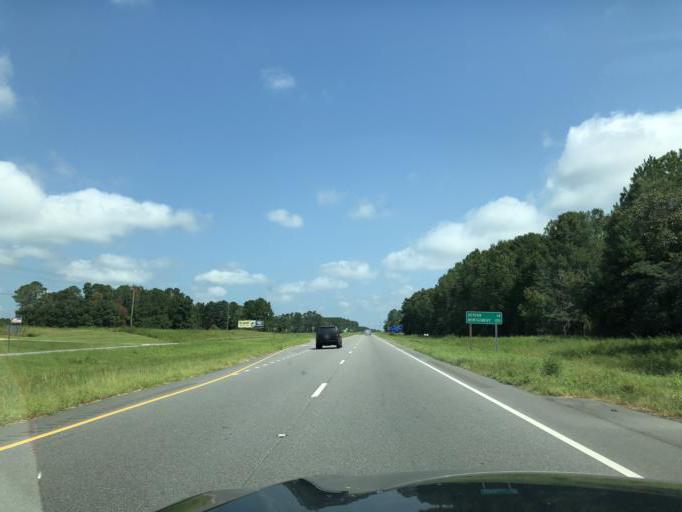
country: US
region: Alabama
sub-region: Houston County
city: Cottonwood
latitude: 31.0039
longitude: -85.4077
